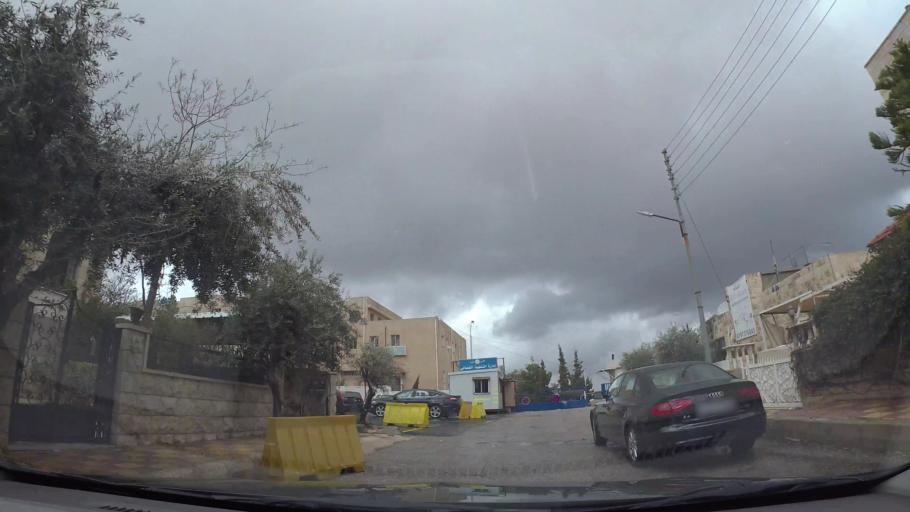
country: JO
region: Amman
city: Amman
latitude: 31.9979
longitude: 35.9245
